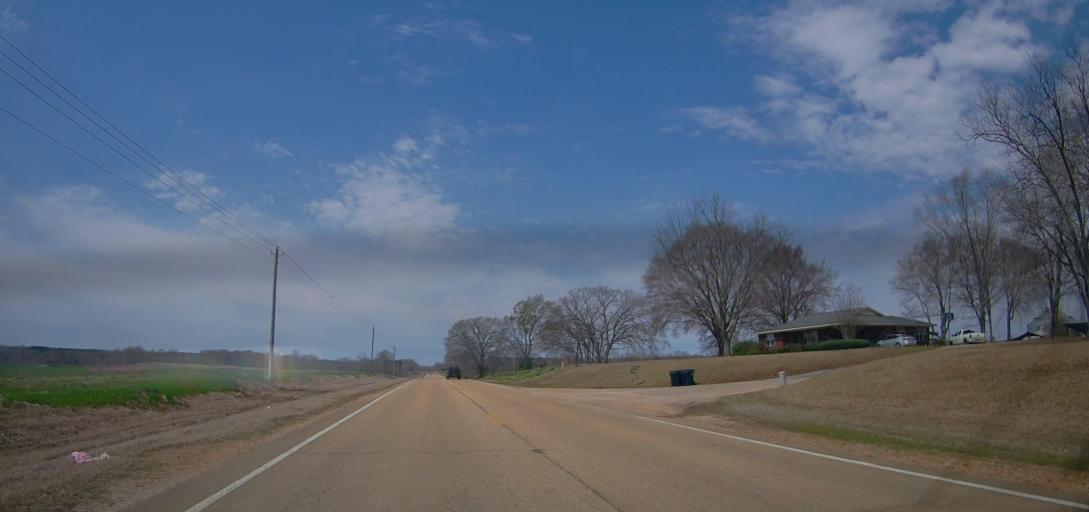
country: US
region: Mississippi
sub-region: Benton County
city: Ashland
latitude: 34.6206
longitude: -89.2302
